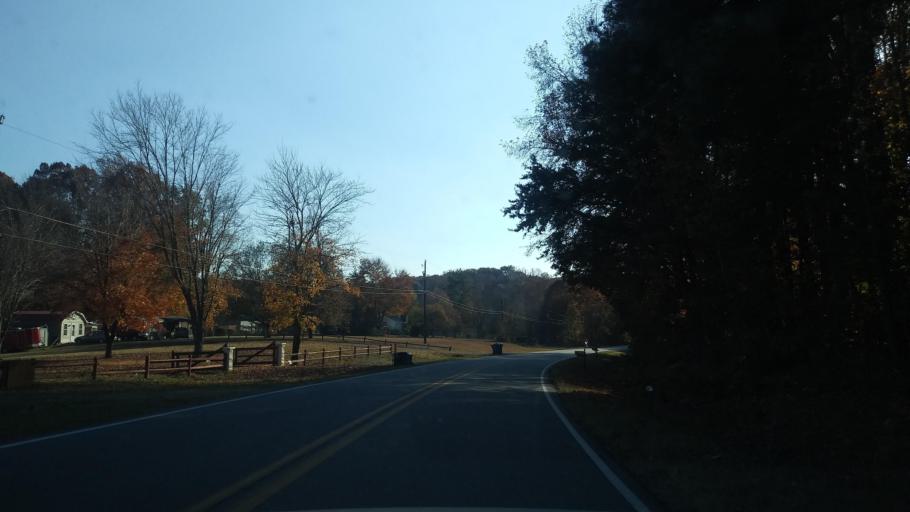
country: US
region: North Carolina
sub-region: Rockingham County
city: Reidsville
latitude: 36.2358
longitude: -79.7167
